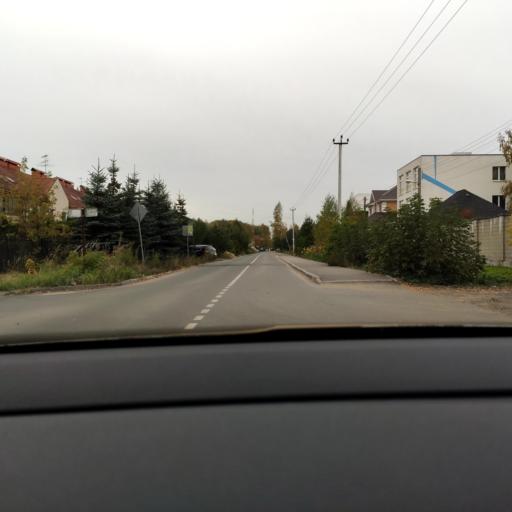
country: RU
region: Moskovskaya
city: Zagoryanskiy
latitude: 55.9646
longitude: 37.9614
